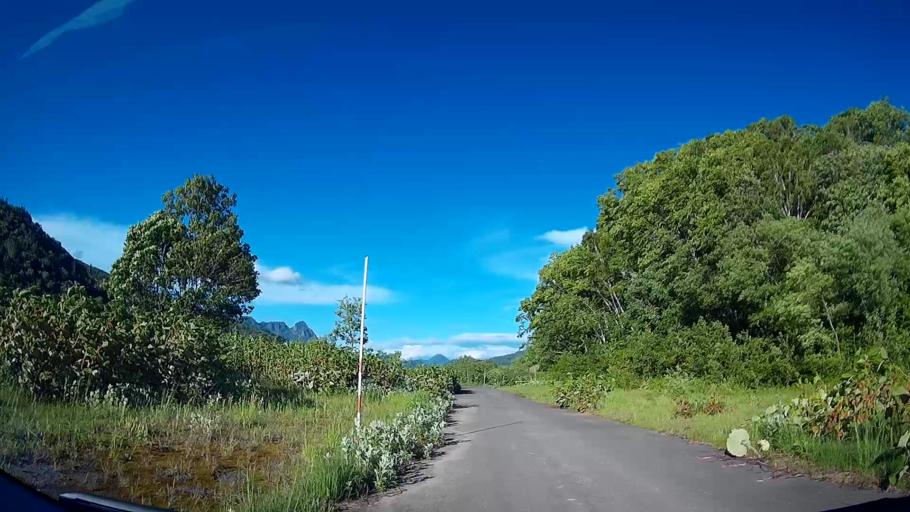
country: JP
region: Hokkaido
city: Otaru
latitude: 42.9804
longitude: 141.0432
